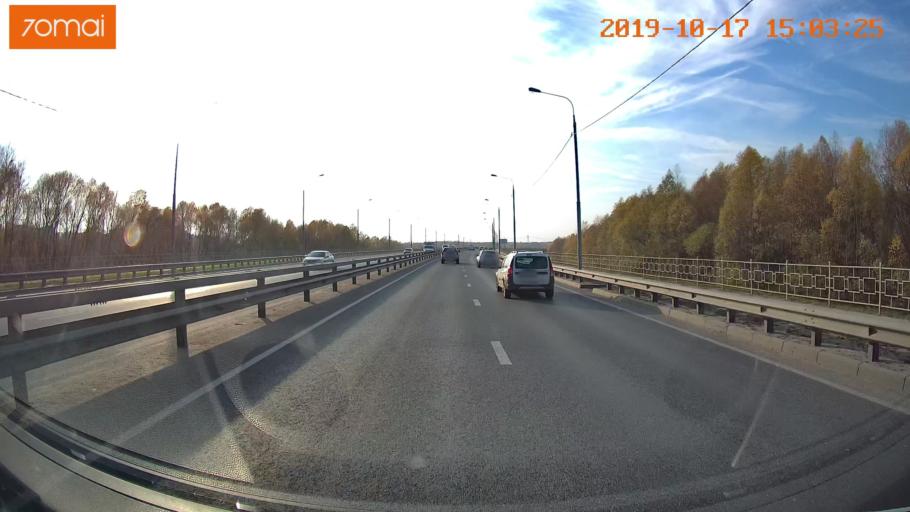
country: RU
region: Rjazan
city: Ryazan'
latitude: 54.6420
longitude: 39.7308
